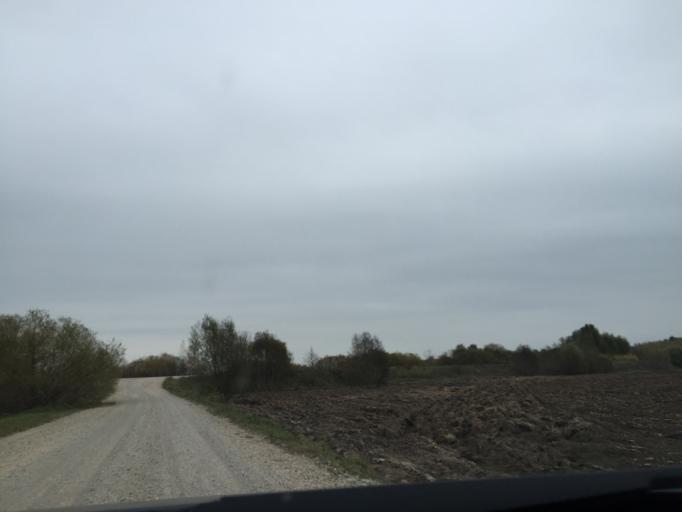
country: LV
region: Ozolnieku
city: Ozolnieki
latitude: 56.6390
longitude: 23.7885
